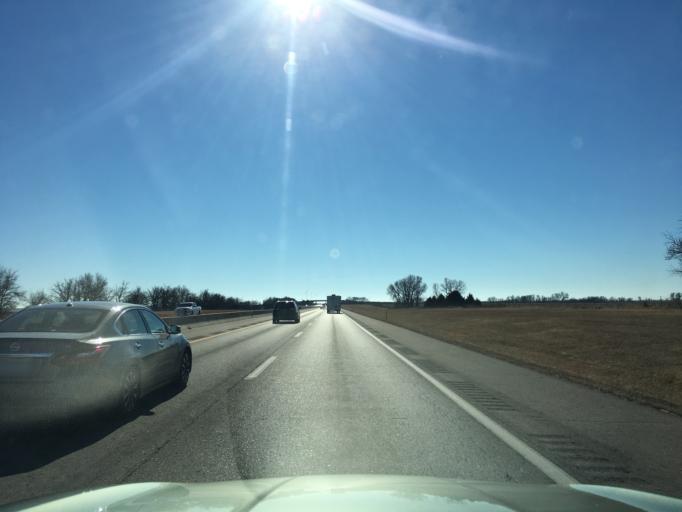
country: US
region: Kansas
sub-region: Sumner County
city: Wellington
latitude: 37.0362
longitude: -97.3383
